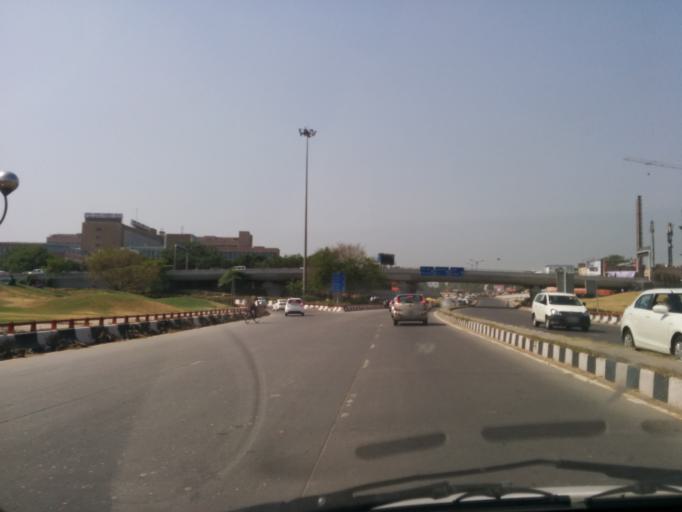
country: IN
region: NCT
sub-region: New Delhi
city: New Delhi
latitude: 28.5706
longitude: 77.2090
